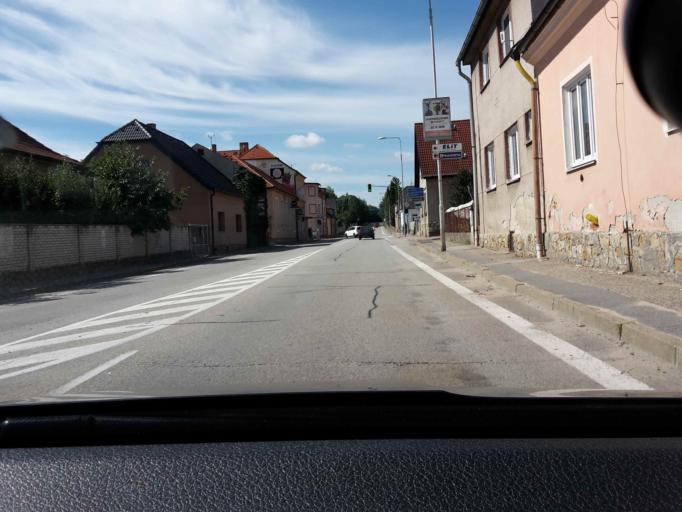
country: CZ
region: Jihocesky
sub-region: Okres Jindrichuv Hradec
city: Jindrichuv Hradec
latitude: 49.1540
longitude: 14.9985
